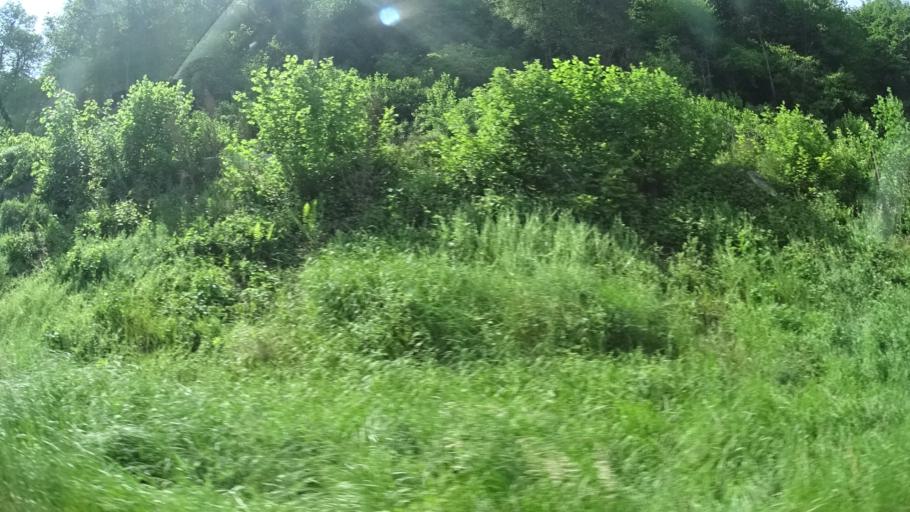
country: DE
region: Bavaria
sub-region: Regierungsbezirk Unterfranken
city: Dorfprozelten
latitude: 49.7793
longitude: 9.3675
